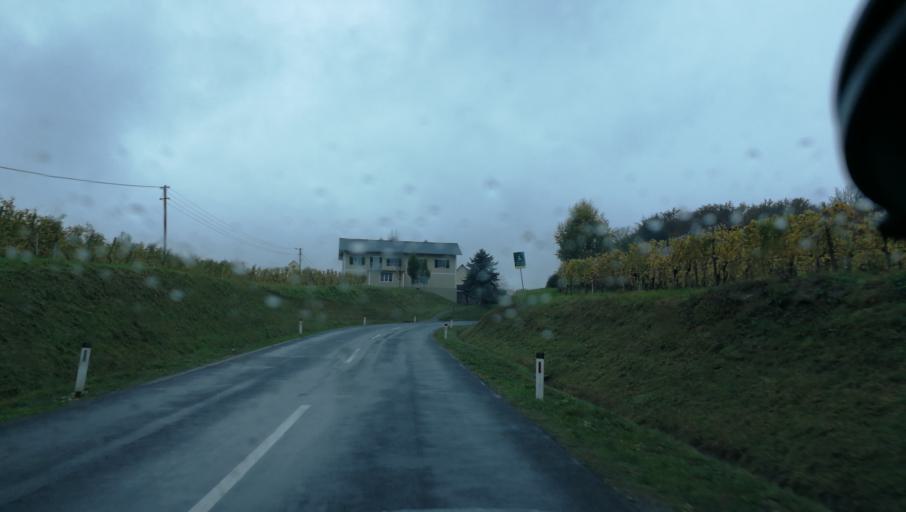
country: AT
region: Styria
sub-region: Politischer Bezirk Leibnitz
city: Spielfeld
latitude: 46.7024
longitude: 15.6228
